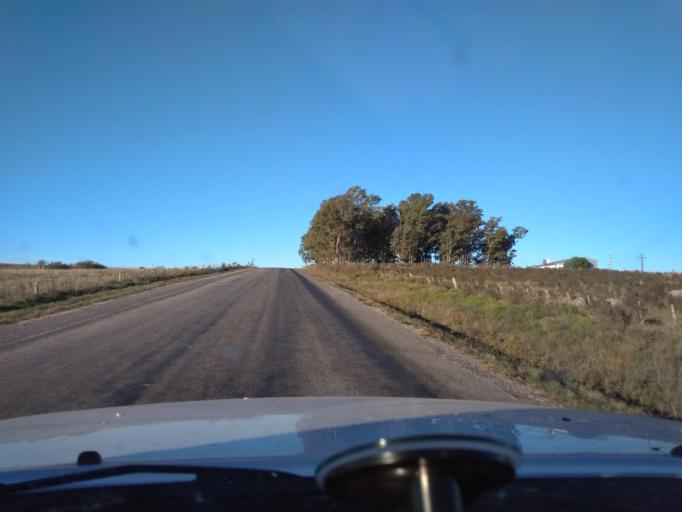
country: UY
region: Florida
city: Casupa
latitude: -34.0074
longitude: -55.8131
